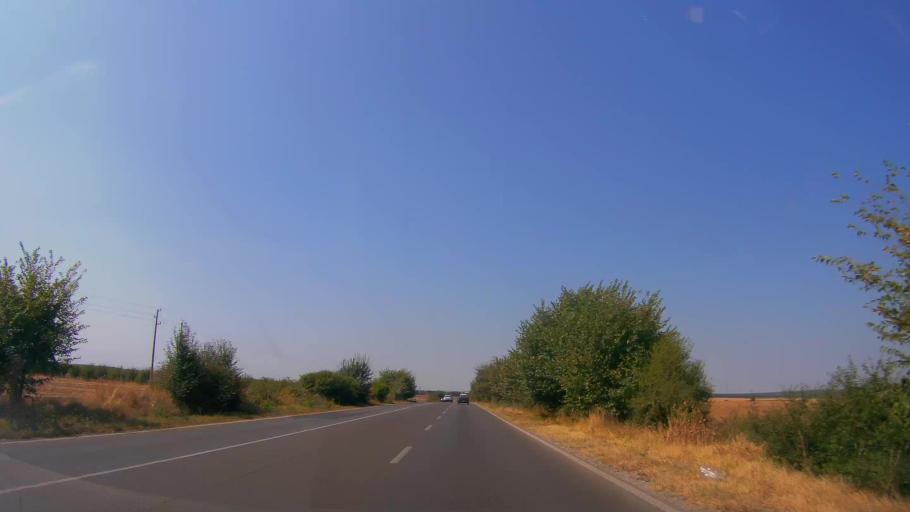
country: BG
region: Ruse
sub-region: Obshtina Vetovo
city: Senovo
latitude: 43.5646
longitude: 26.3377
